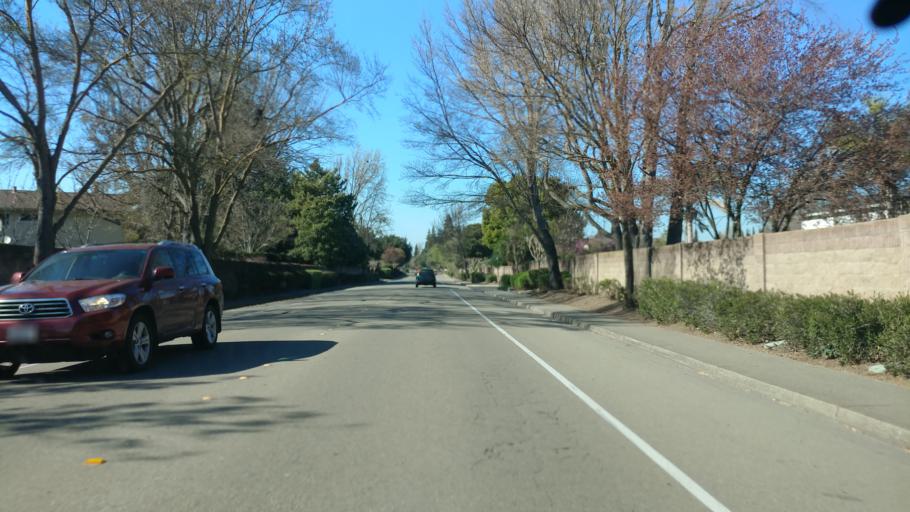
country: US
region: California
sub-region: Contra Costa County
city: San Ramon
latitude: 37.7847
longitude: -121.9763
